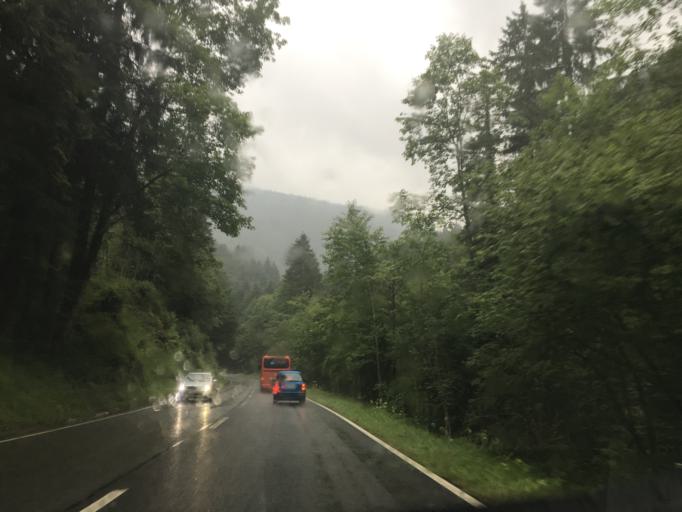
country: DE
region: Bavaria
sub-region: Upper Bavaria
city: Reit im Winkl
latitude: 47.7028
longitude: 12.4785
